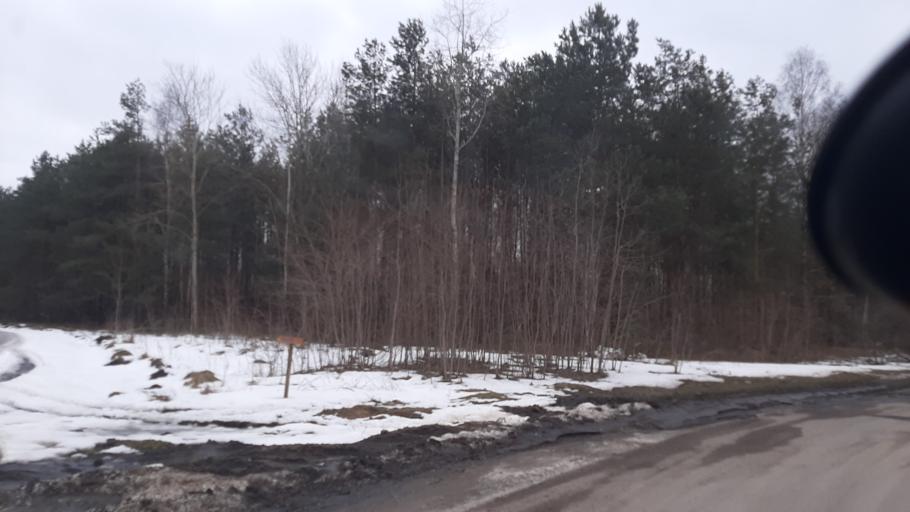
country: PL
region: Lublin Voivodeship
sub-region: Powiat wlodawski
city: Wlodawa
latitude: 51.5181
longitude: 23.5922
